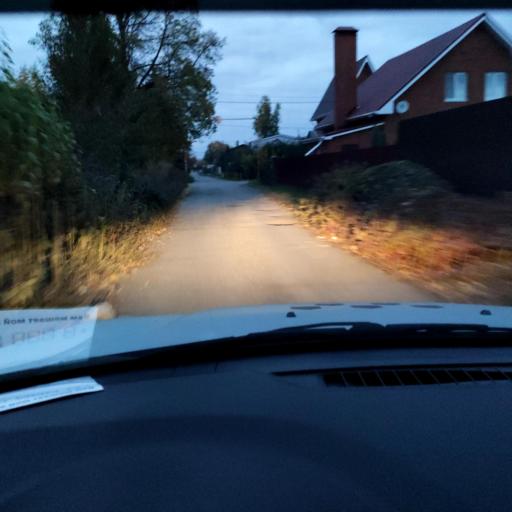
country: RU
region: Samara
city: Tol'yatti
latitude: 53.5251
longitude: 49.4087
